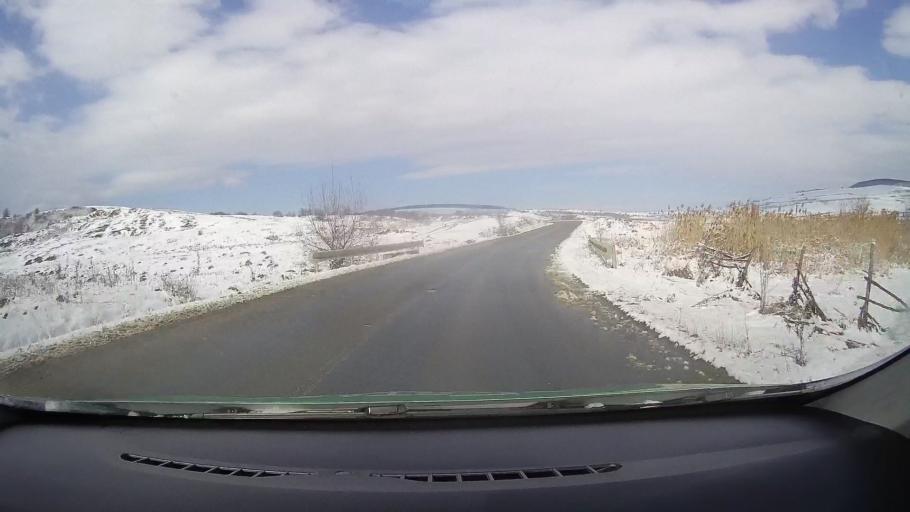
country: RO
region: Sibiu
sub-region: Comuna Altina
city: Altina
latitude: 45.9408
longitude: 24.4540
